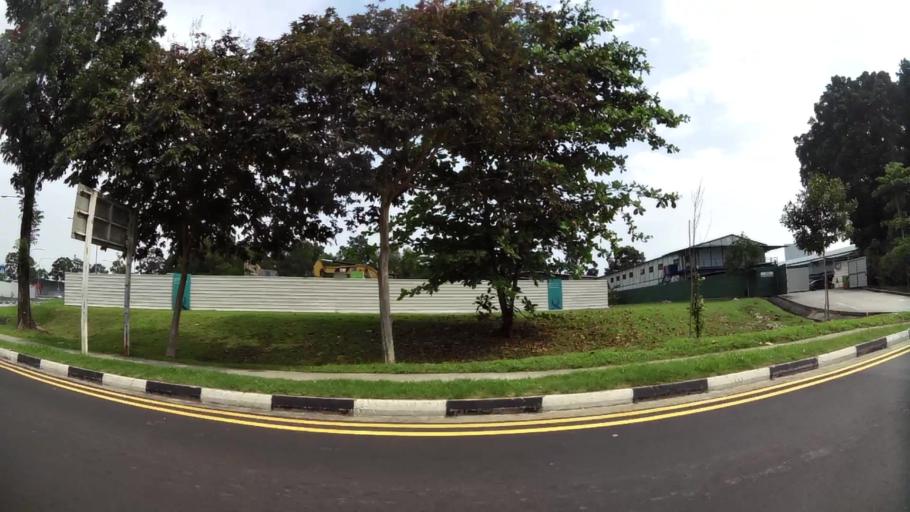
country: SG
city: Singapore
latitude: 1.3380
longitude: 103.9601
